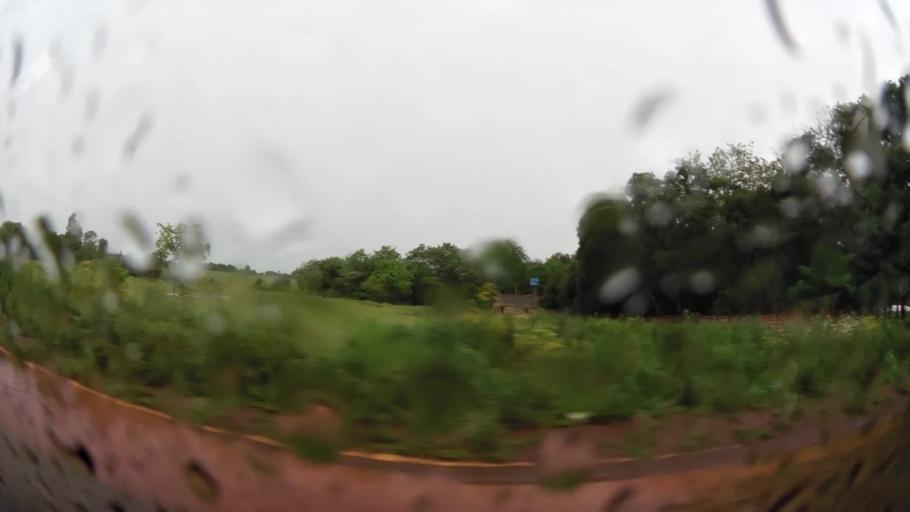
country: PY
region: Alto Parana
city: Presidente Franco
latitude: -25.5276
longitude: -54.6785
